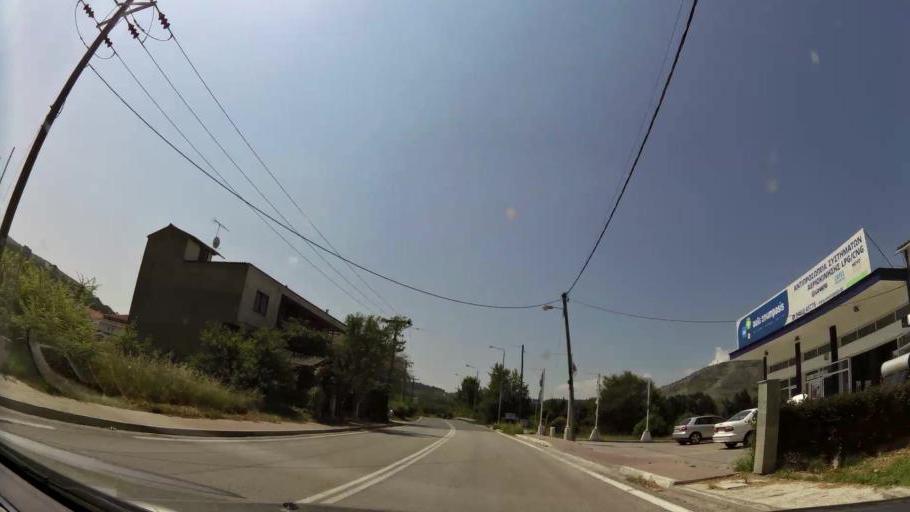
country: GR
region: West Macedonia
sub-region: Nomos Kozanis
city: Koila
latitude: 40.3292
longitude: 21.7886
